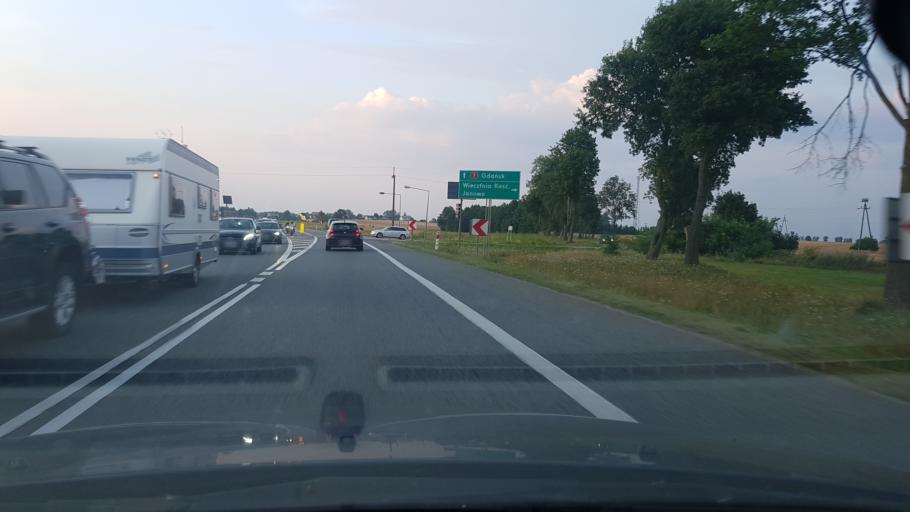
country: PL
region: Masovian Voivodeship
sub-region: Powiat mlawski
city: Wieczfnia Koscielna
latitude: 53.1781
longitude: 20.4285
